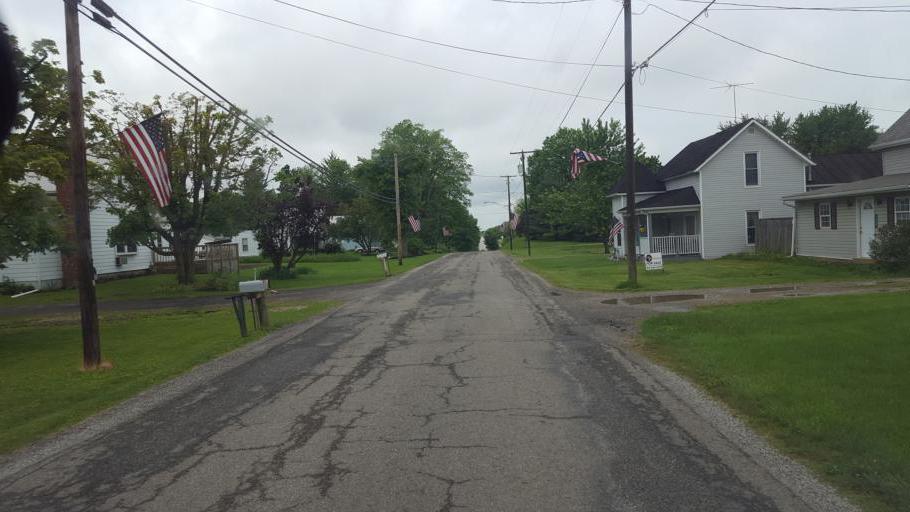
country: US
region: Ohio
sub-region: Morrow County
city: Cardington
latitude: 40.4633
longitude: -82.8325
